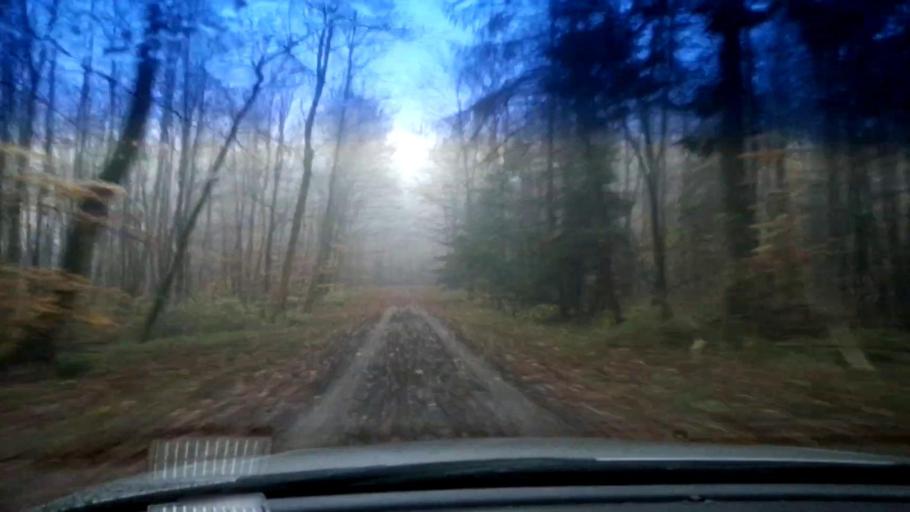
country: DE
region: Bavaria
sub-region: Upper Franconia
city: Schesslitz
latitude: 49.9355
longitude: 11.0599
